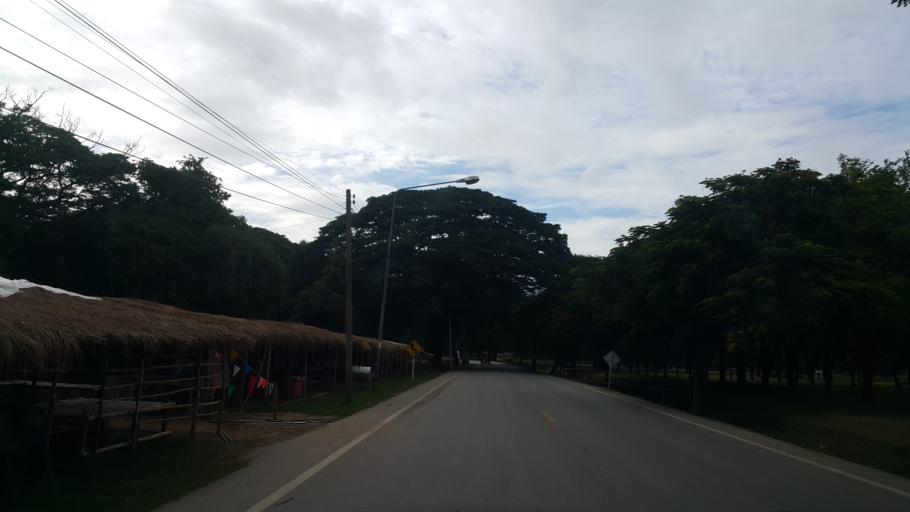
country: TH
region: Sukhothai
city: Ban Na
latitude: 17.0217
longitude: 99.7042
